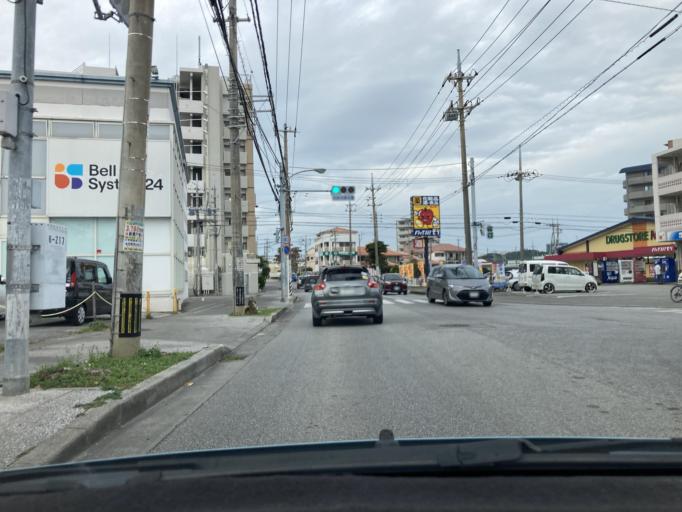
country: JP
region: Okinawa
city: Chatan
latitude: 26.3086
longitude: 127.7617
